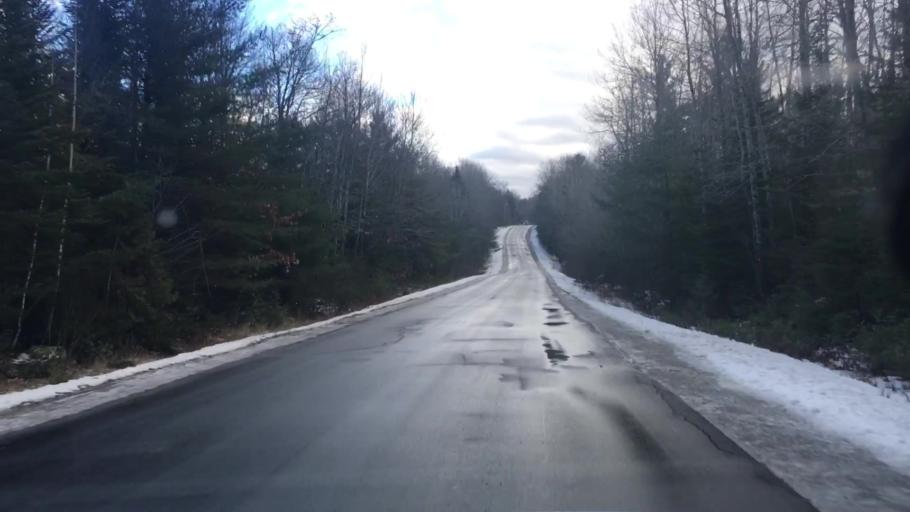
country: US
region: Maine
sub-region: Hancock County
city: Dedham
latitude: 44.6885
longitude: -68.7149
